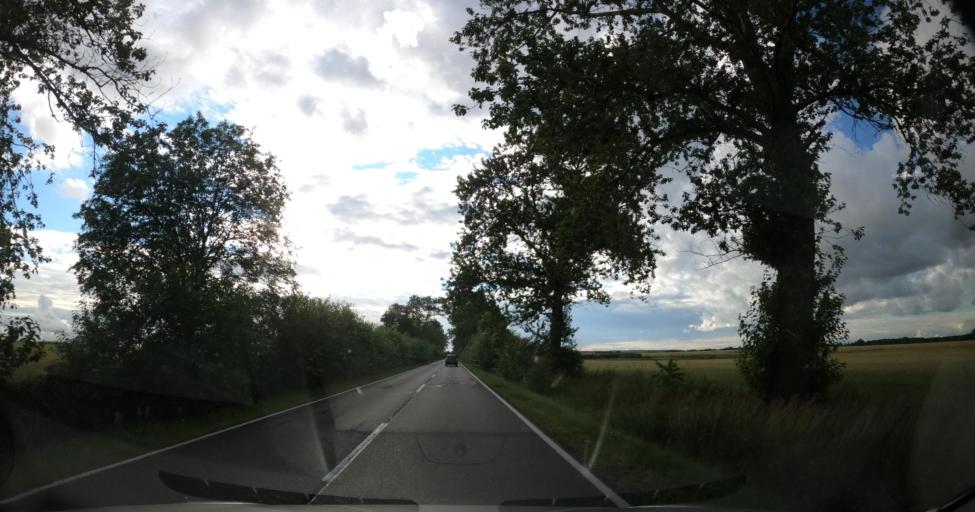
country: PL
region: Pomeranian Voivodeship
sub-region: Powiat slupski
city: Damnica
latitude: 54.4261
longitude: 17.3706
